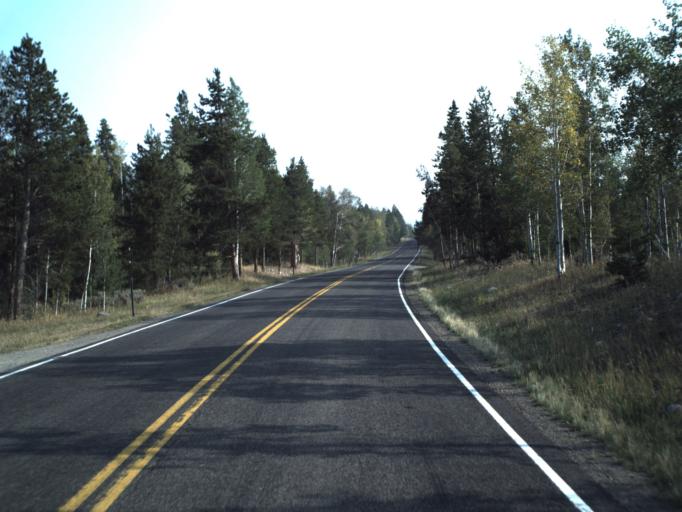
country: US
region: Wyoming
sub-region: Uinta County
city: Evanston
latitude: 40.9280
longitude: -110.8289
